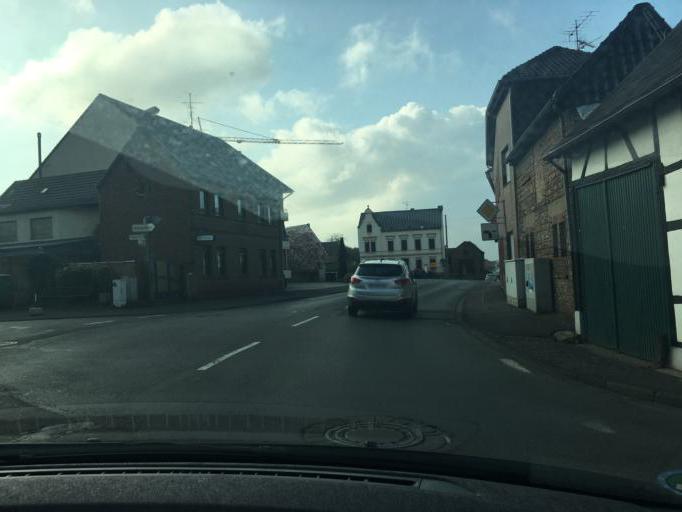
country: DE
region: North Rhine-Westphalia
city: Bornheim
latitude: 50.7637
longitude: 6.9850
